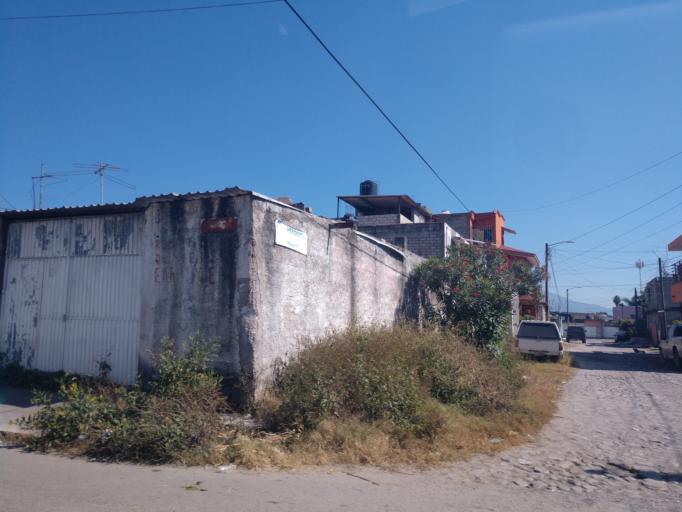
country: MX
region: Nayarit
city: Xalisco
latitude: 21.4673
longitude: -104.8771
